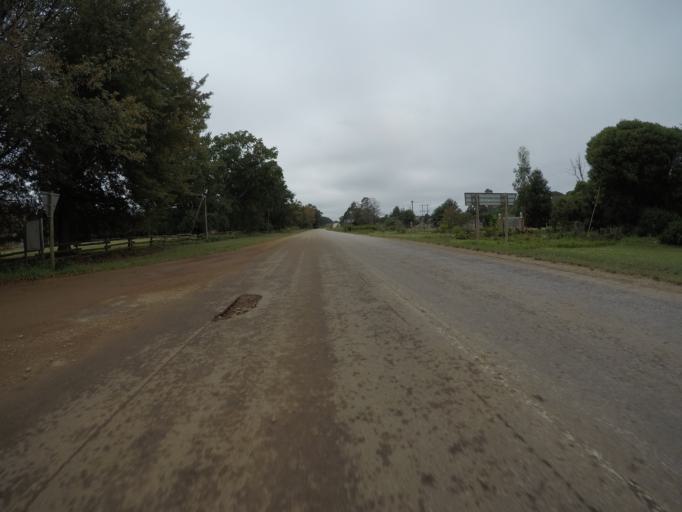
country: ZA
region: Eastern Cape
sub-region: Cacadu District Municipality
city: Kareedouw
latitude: -33.9944
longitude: 24.1178
